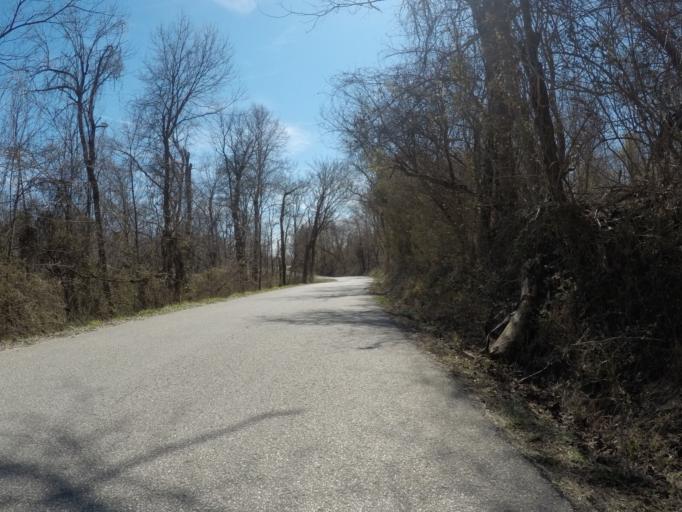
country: US
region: West Virginia
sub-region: Cabell County
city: Huntington
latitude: 38.4560
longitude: -82.4930
